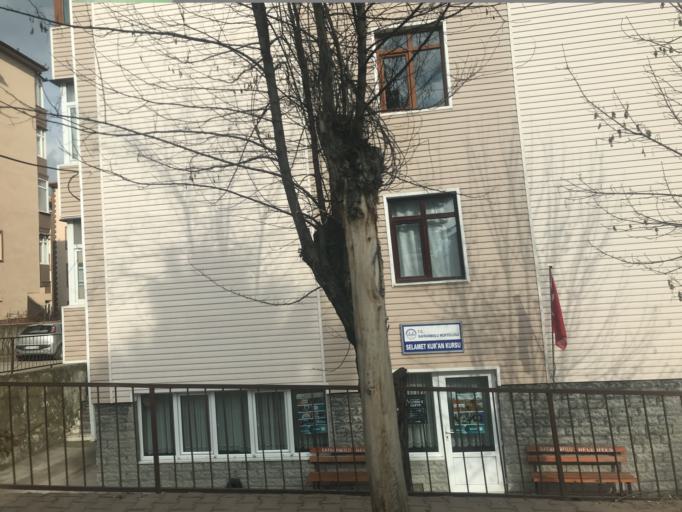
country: TR
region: Karabuk
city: Safranbolu
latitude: 41.2560
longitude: 32.6817
